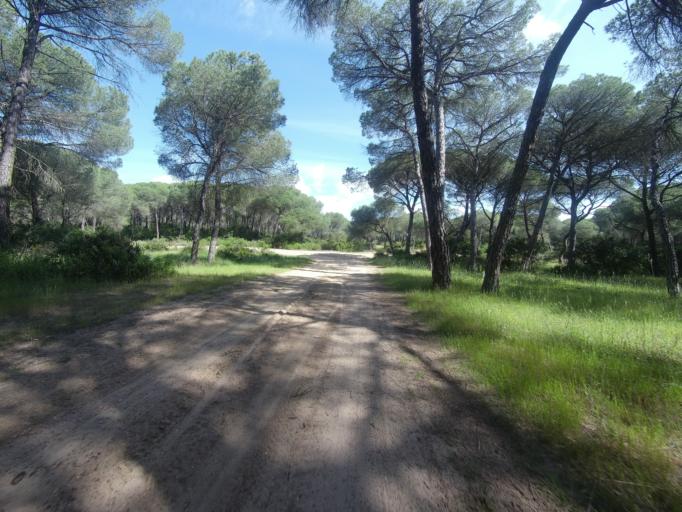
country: ES
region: Andalusia
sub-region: Provincia de Huelva
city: Aljaraque
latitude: 37.2352
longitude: -7.0505
